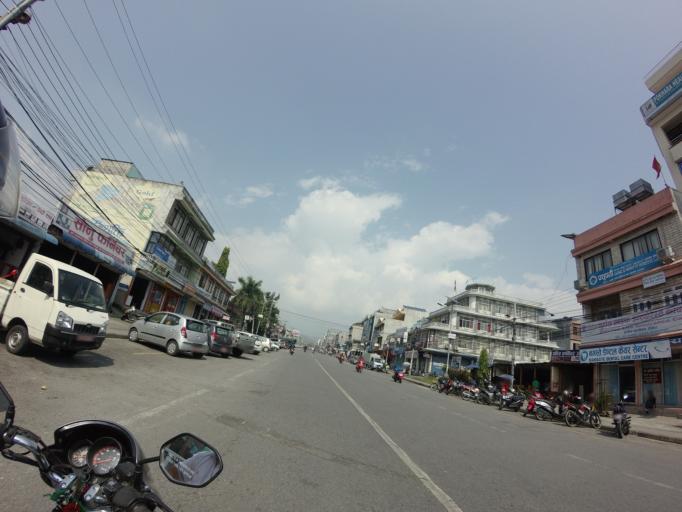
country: NP
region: Western Region
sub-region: Gandaki Zone
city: Pokhara
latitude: 28.2171
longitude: 83.9863
